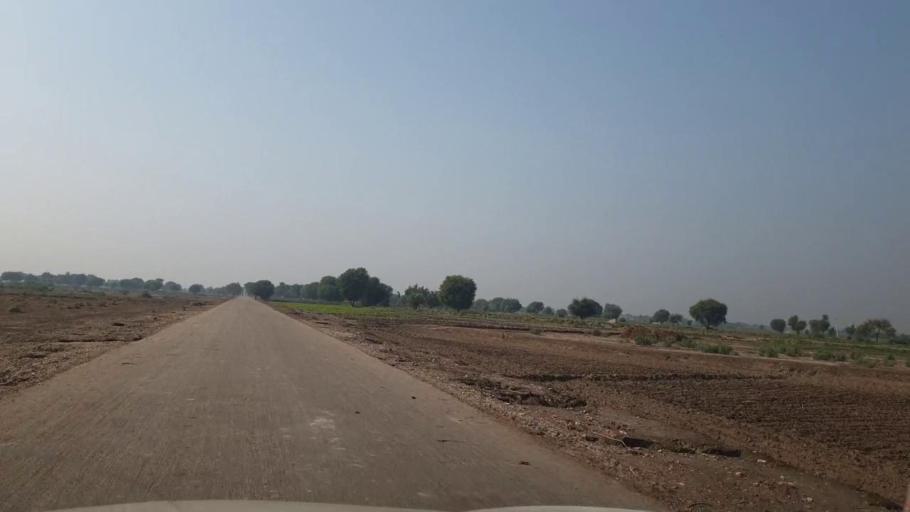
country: PK
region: Sindh
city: Bhan
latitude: 26.5231
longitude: 67.8090
